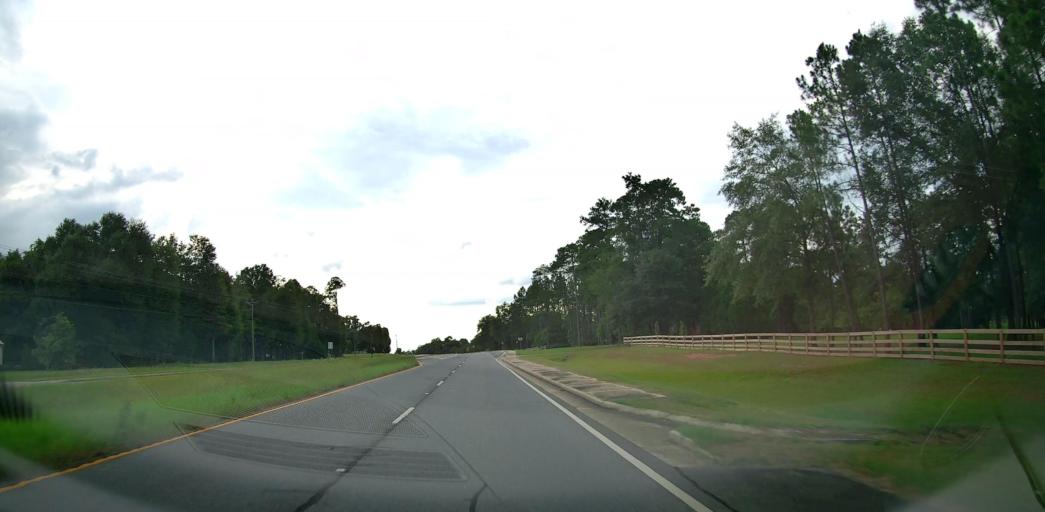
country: US
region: Georgia
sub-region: Pulaski County
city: Hawkinsville
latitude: 32.2770
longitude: -83.4252
